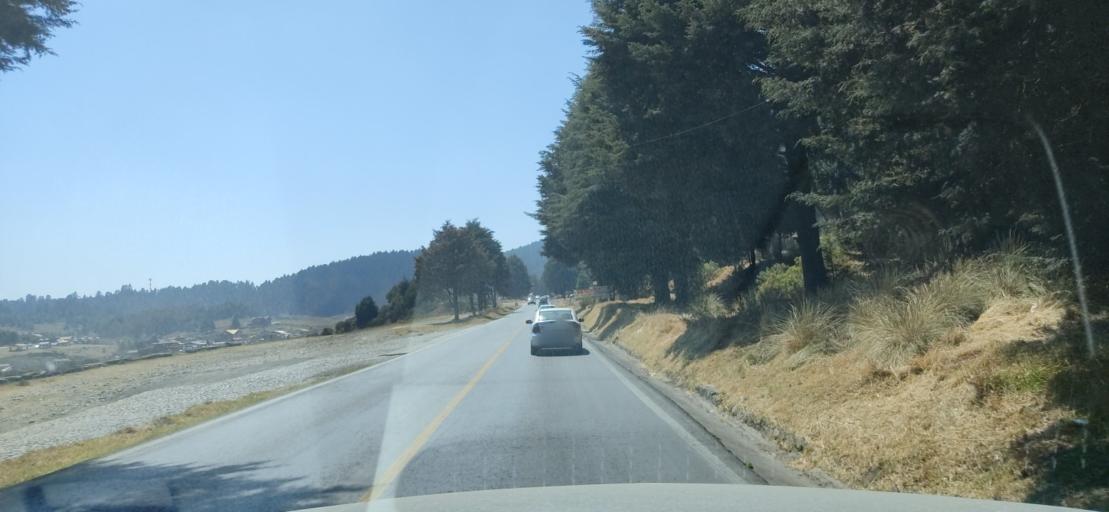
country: MX
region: Mexico
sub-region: Ocoyoacac
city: San Jeronimo Acazulco
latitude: 19.2864
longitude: -99.3738
